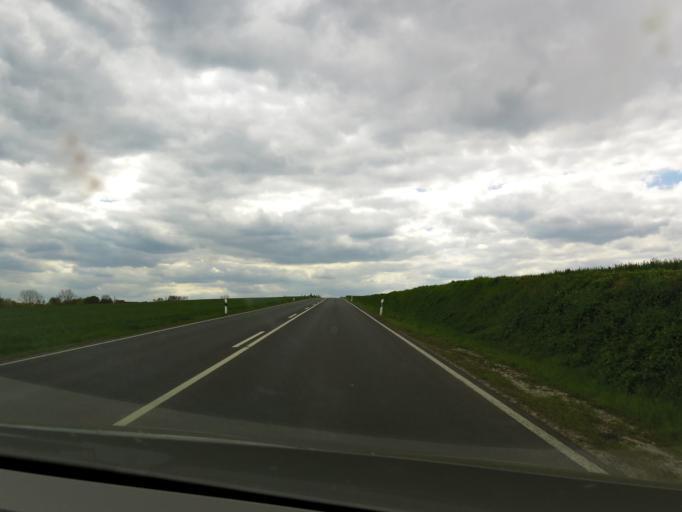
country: DE
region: Thuringia
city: Rannstedt
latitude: 51.0930
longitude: 11.5425
